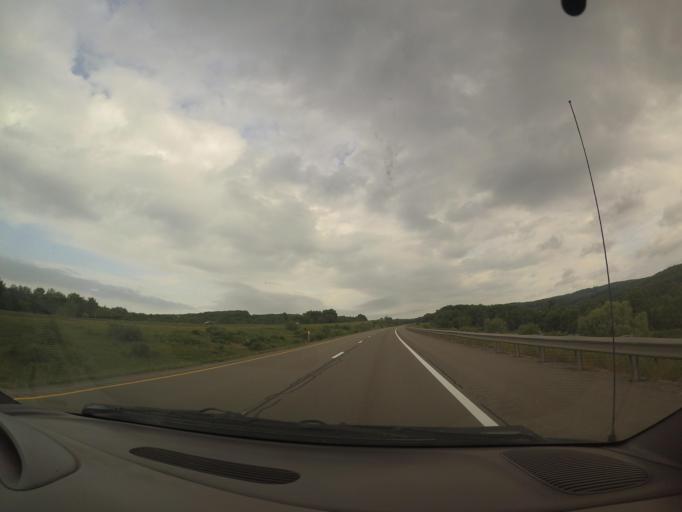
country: US
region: New York
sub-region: Allegany County
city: Alfred
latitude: 42.3182
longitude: -77.8209
